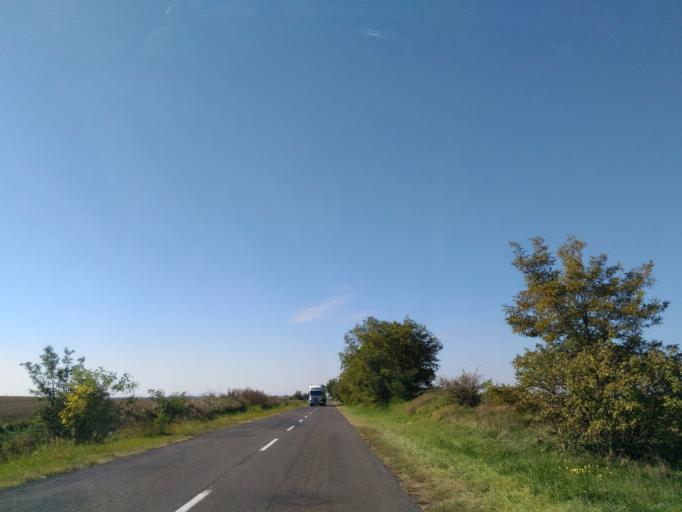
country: HU
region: Fejer
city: Ivancsa
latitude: 47.1756
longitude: 18.7995
